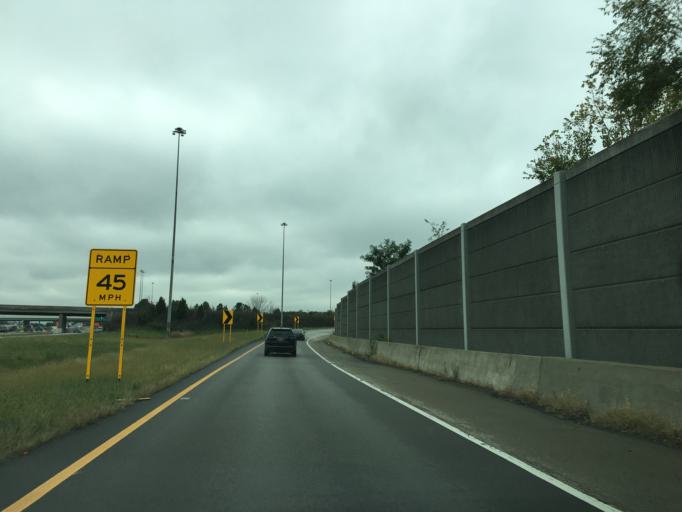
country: US
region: Ohio
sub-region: Hamilton County
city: Glendale
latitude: 39.2950
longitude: -84.4420
